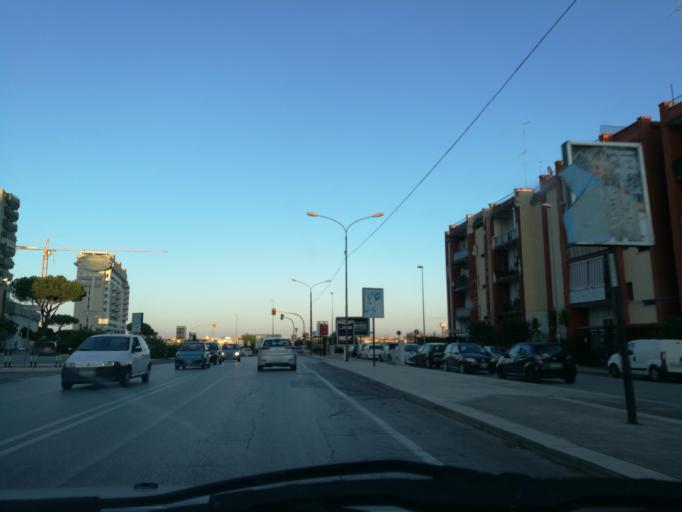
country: IT
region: Apulia
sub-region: Provincia di Bari
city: San Paolo
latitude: 41.1229
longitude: 16.8011
